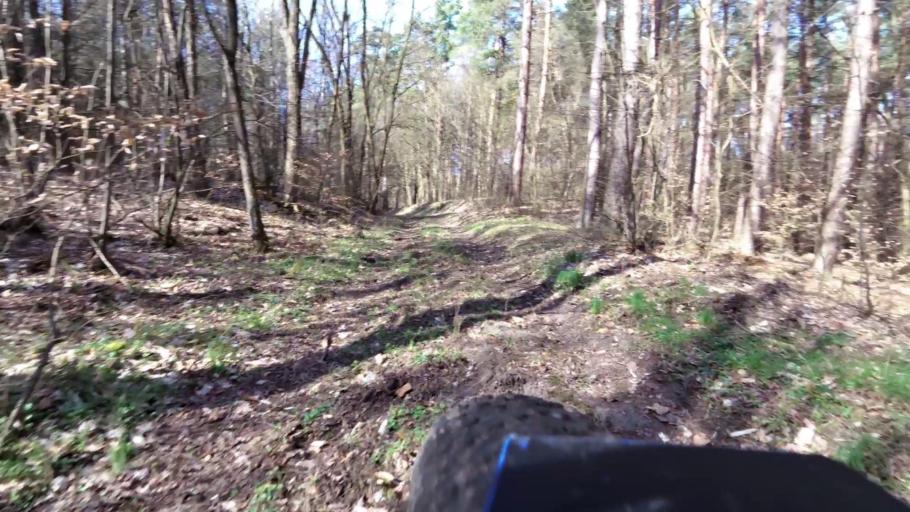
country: PL
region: Lubusz
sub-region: Powiat slubicki
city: Cybinka
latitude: 52.2090
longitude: 14.8706
